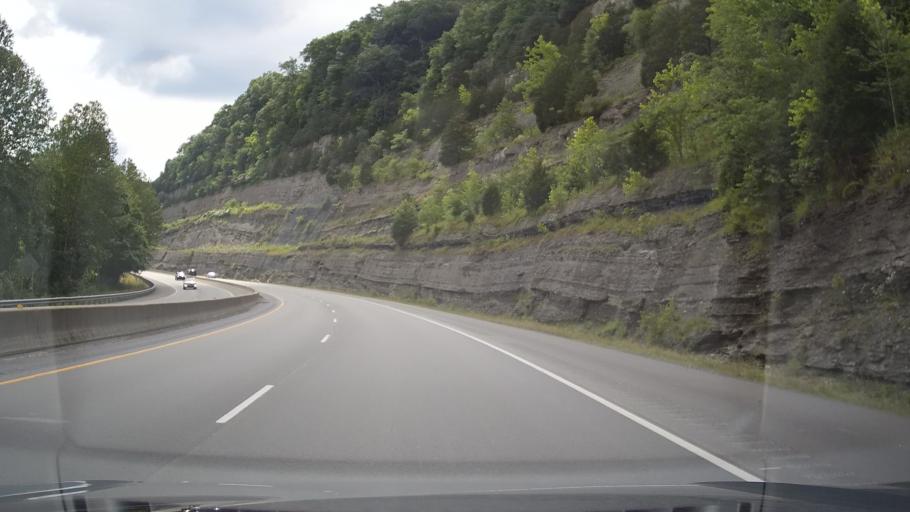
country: US
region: Kentucky
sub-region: Floyd County
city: Prestonsburg
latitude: 37.5946
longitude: -82.6660
